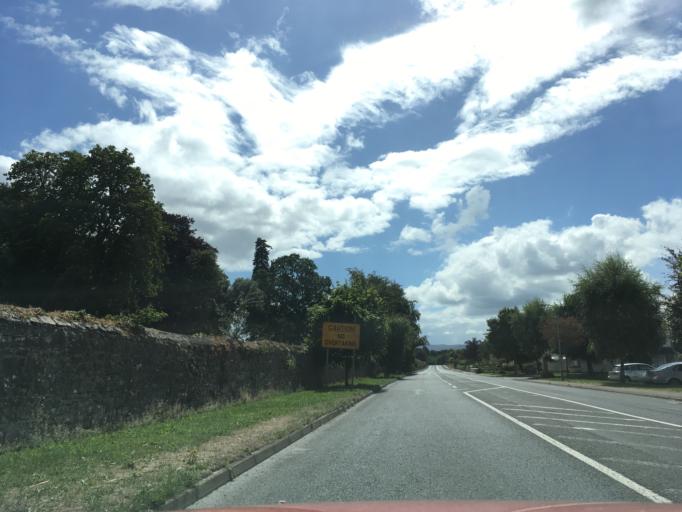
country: IE
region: Munster
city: Cahir
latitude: 52.3714
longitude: -7.9311
